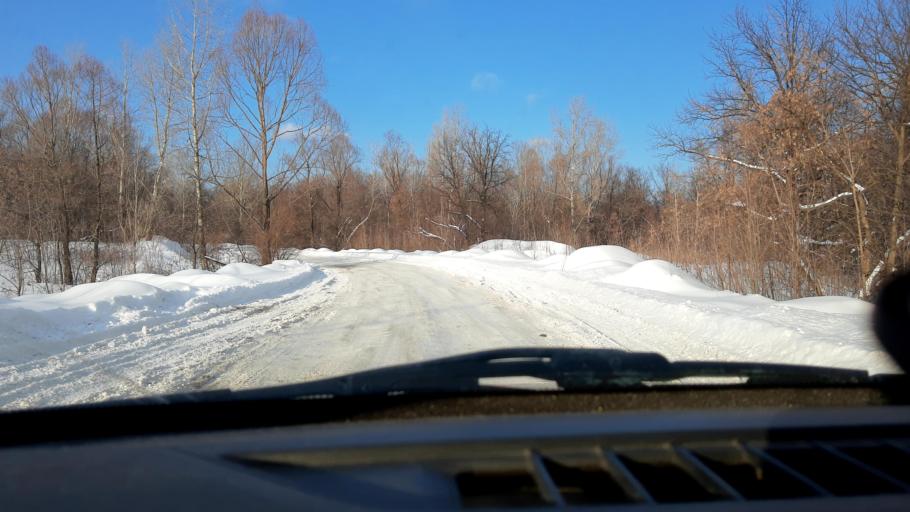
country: RU
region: Bashkortostan
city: Ufa
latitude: 54.6374
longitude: 56.0060
